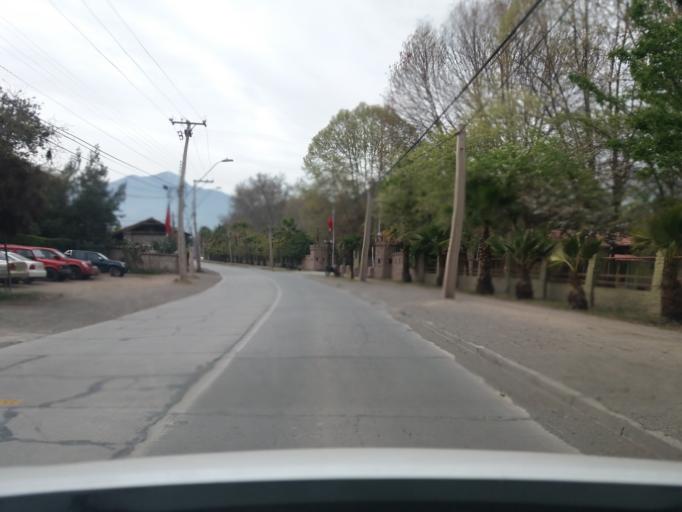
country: CL
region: Valparaiso
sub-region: Provincia de Los Andes
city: Los Andes
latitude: -32.8371
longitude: -70.5791
